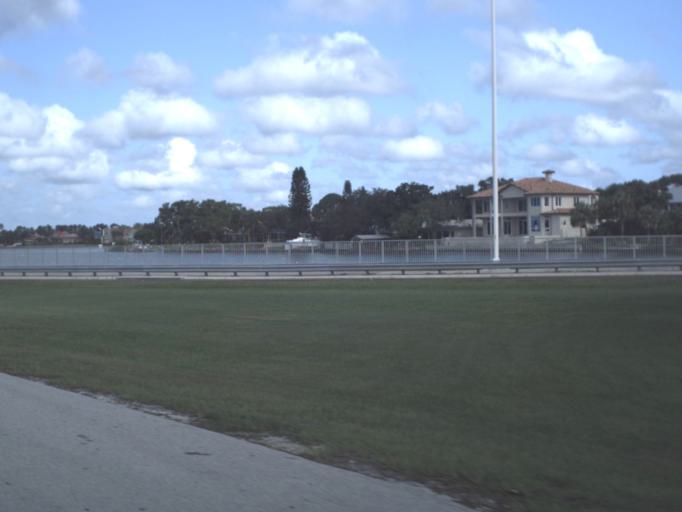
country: US
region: Florida
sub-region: Hillsborough County
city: Town 'n' Country
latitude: 27.9675
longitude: -82.5556
